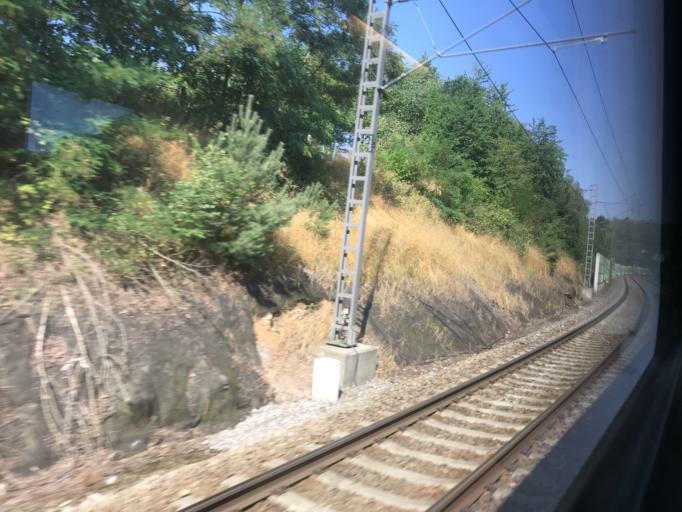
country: CZ
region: Central Bohemia
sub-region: Okres Praha-Vychod
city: Mnichovice
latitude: 49.9284
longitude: 14.7127
